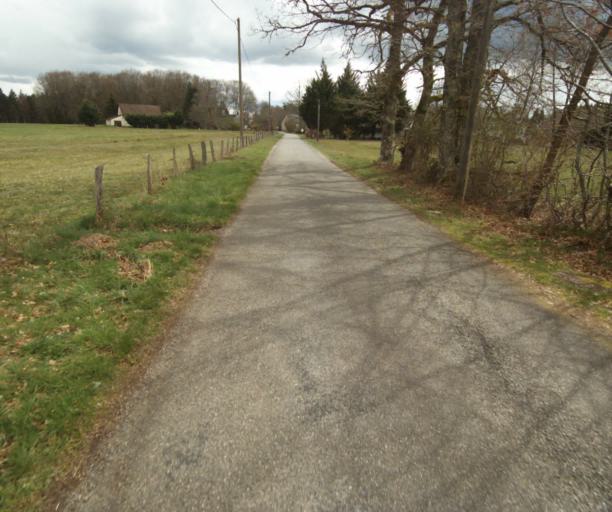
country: FR
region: Limousin
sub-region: Departement de la Correze
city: Correze
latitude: 45.2758
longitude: 1.9798
